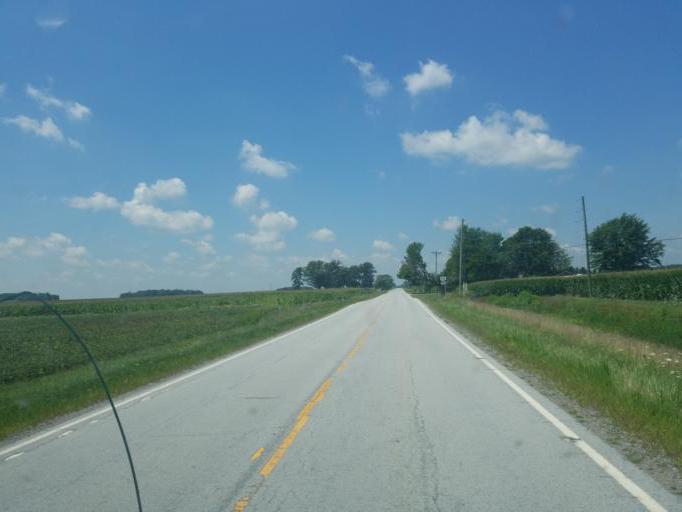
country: US
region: Ohio
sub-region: Allen County
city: Spencerville
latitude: 40.7140
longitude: -84.4218
